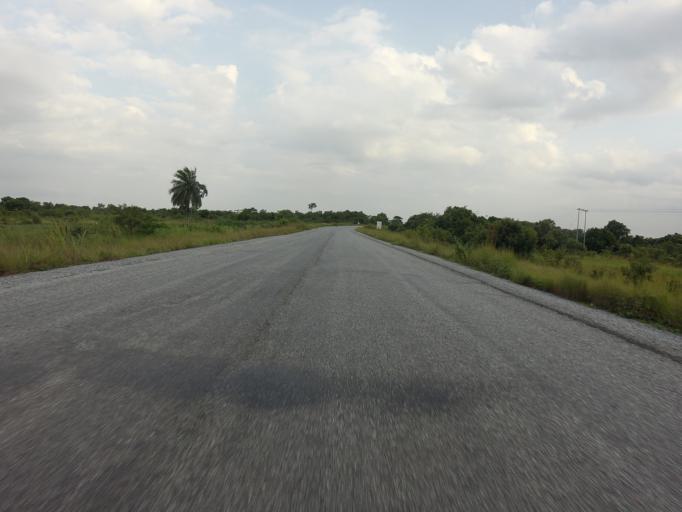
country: GH
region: Volta
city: Ho
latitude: 6.3680
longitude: 0.5343
